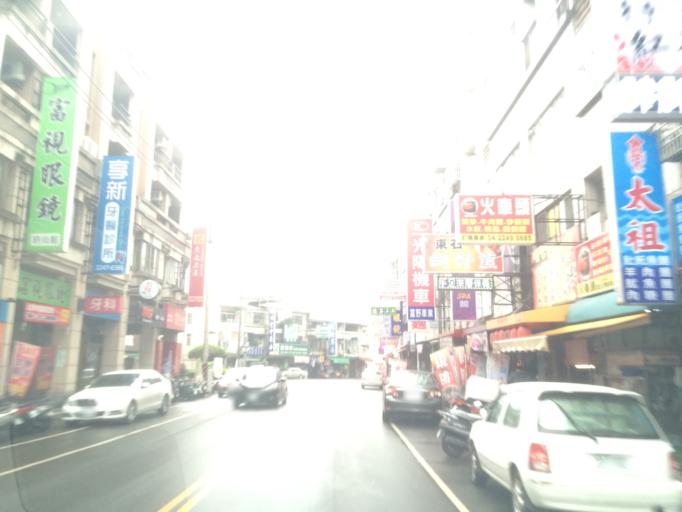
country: TW
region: Taiwan
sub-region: Taichung City
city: Taichung
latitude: 24.1797
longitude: 120.6902
